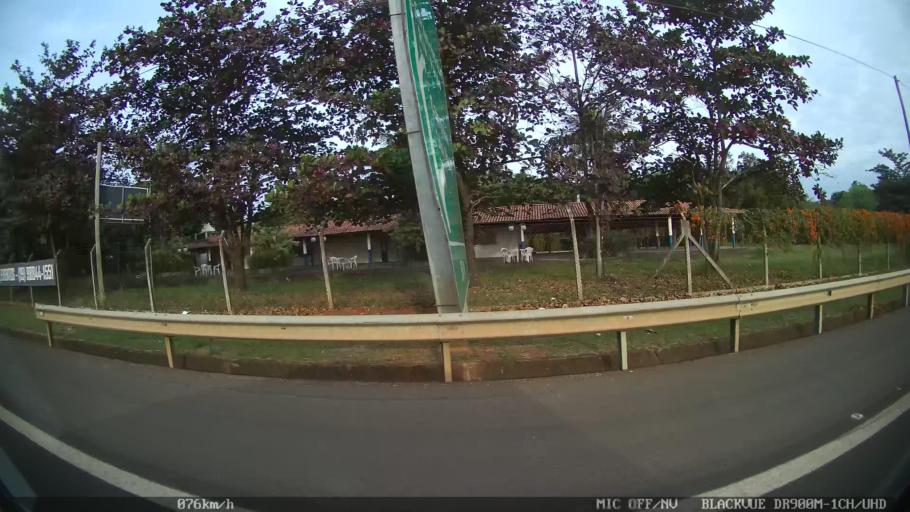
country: BR
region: Sao Paulo
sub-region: Iracemapolis
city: Iracemapolis
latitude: -22.5937
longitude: -47.4654
